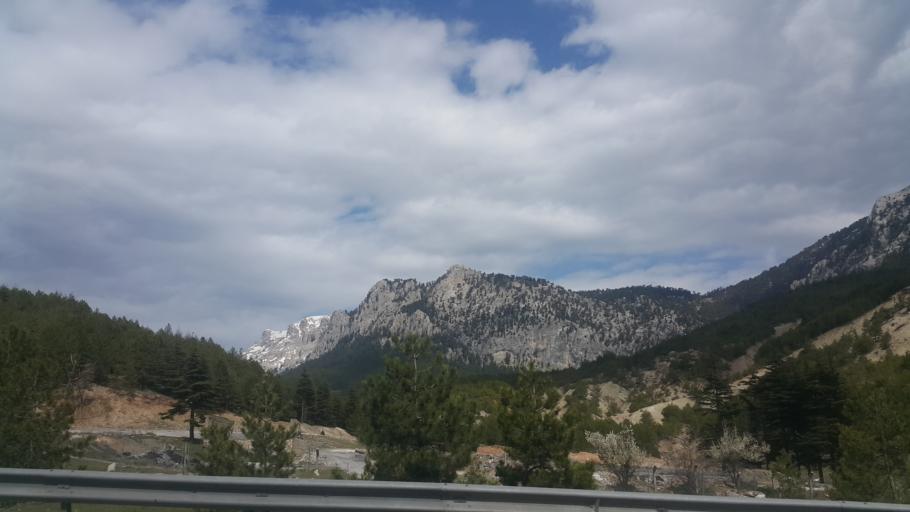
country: TR
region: Adana
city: Pozanti
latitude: 37.3202
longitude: 34.7919
